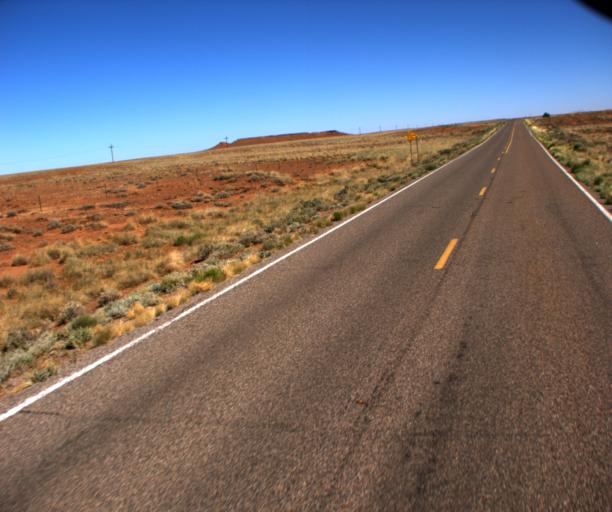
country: US
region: Arizona
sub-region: Coconino County
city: LeChee
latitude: 35.2145
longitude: -110.9510
